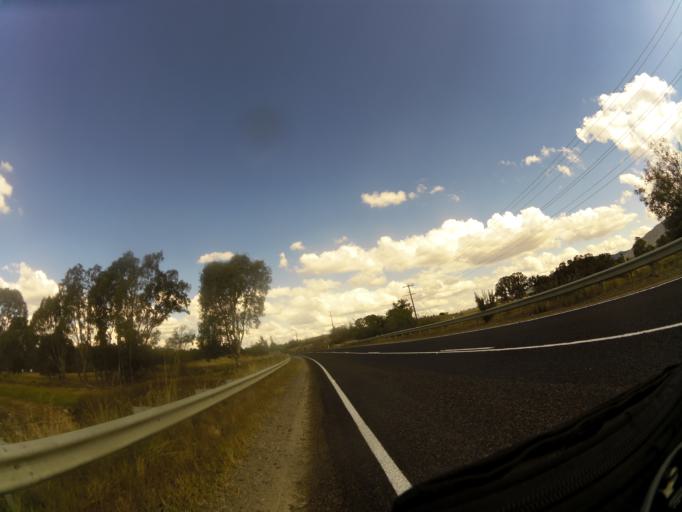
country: AU
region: Victoria
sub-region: Mansfield
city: Mansfield
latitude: -36.9056
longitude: 145.9970
